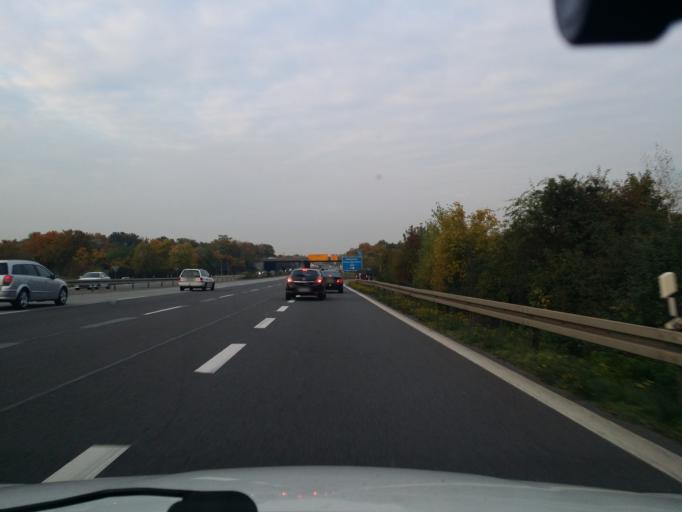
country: DE
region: Rheinland-Pfalz
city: Altrip
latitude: 49.4650
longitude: 8.5165
